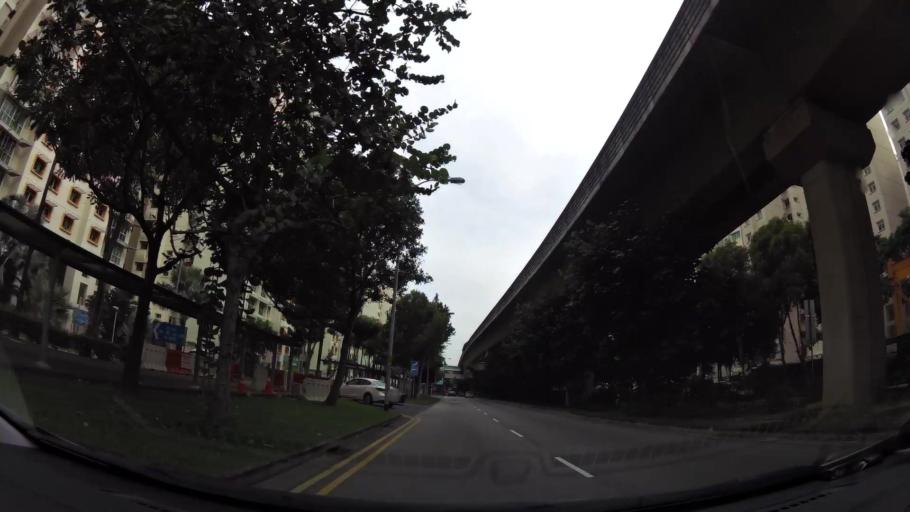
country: MY
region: Johor
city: Kampung Pasir Gudang Baru
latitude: 1.3978
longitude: 103.9079
